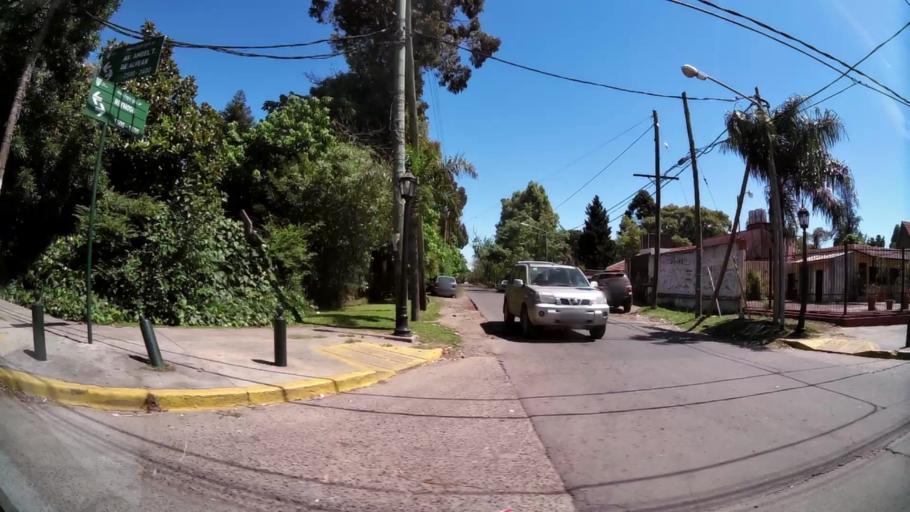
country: AR
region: Buenos Aires
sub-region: Partido de Tigre
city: Tigre
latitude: -34.4890
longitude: -58.6220
